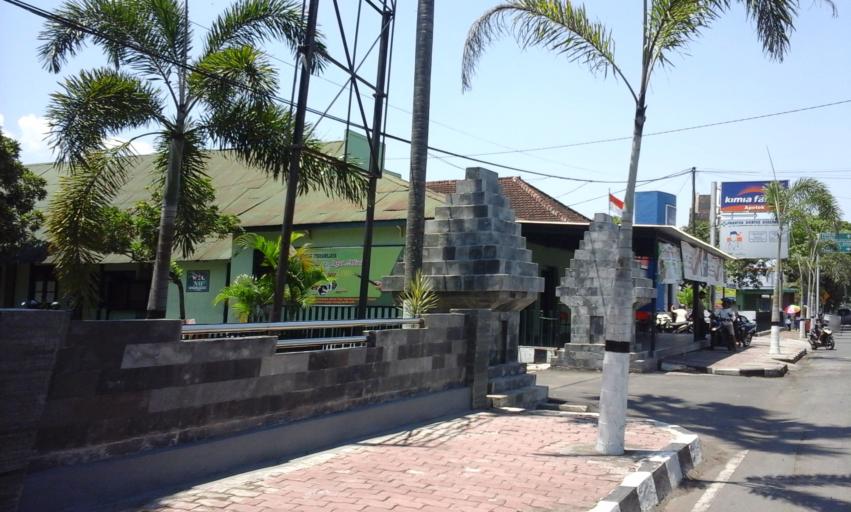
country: ID
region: East Java
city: Krajan
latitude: -8.1653
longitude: 113.7055
